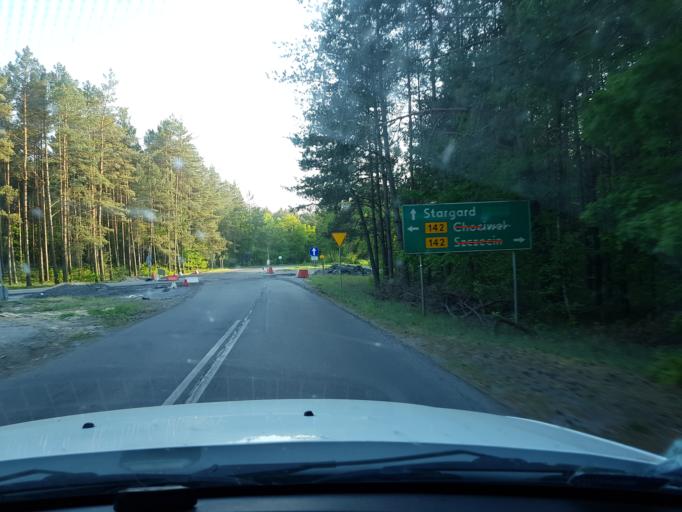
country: PL
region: West Pomeranian Voivodeship
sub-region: Powiat stargardzki
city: Kobylanka
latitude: 53.4421
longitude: 14.9176
